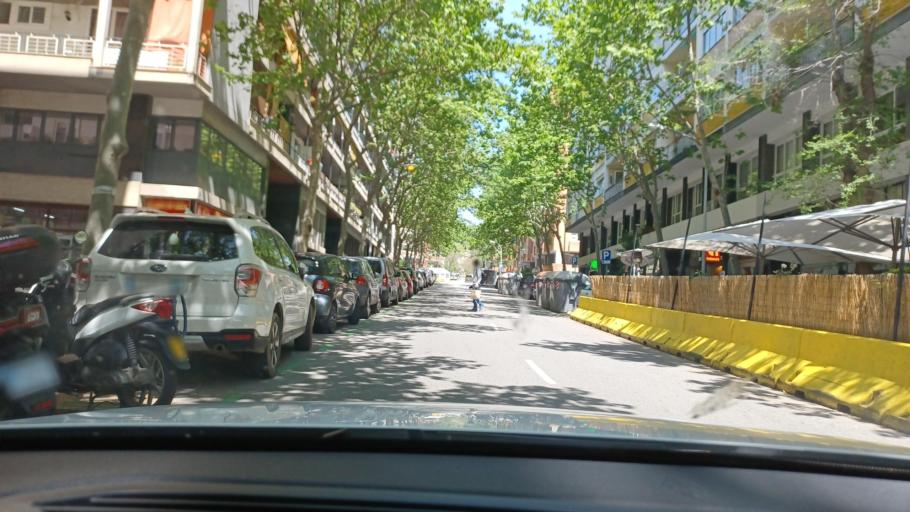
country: ES
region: Catalonia
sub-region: Provincia de Barcelona
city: les Corts
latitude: 41.3920
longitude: 2.1270
